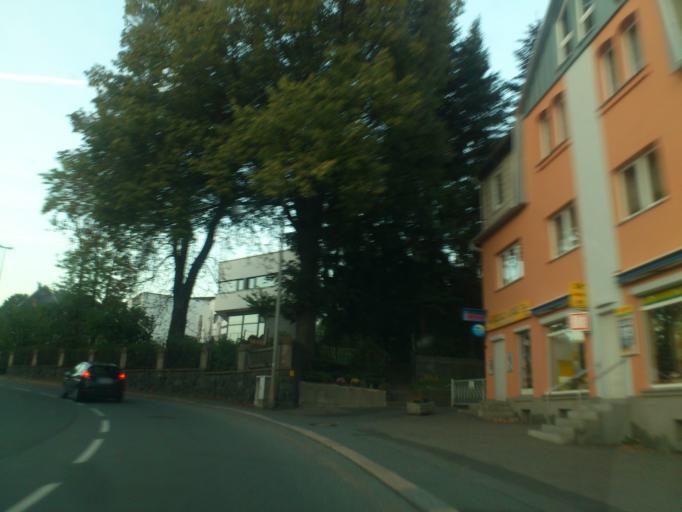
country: DE
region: Saxony
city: Neukirchen
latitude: 50.7797
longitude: 12.8675
